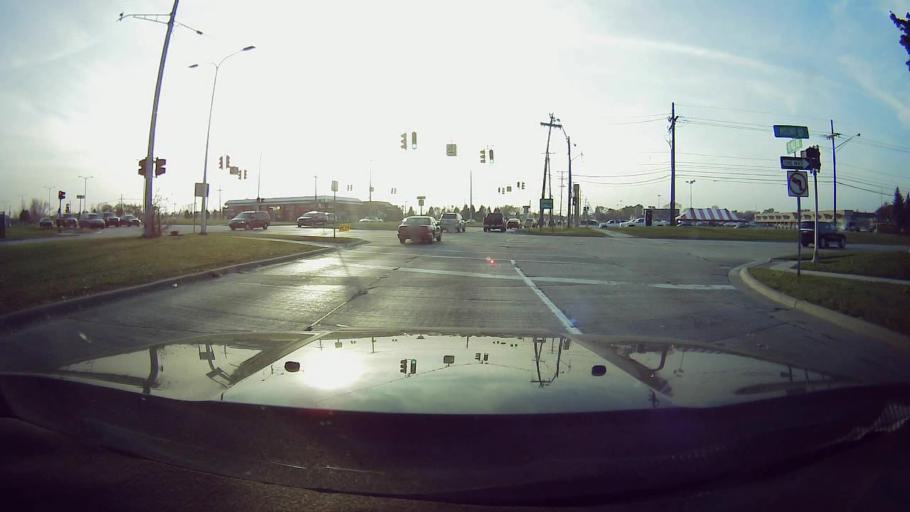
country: US
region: Michigan
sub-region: Macomb County
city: Center Line
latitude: 42.5210
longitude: -83.0468
